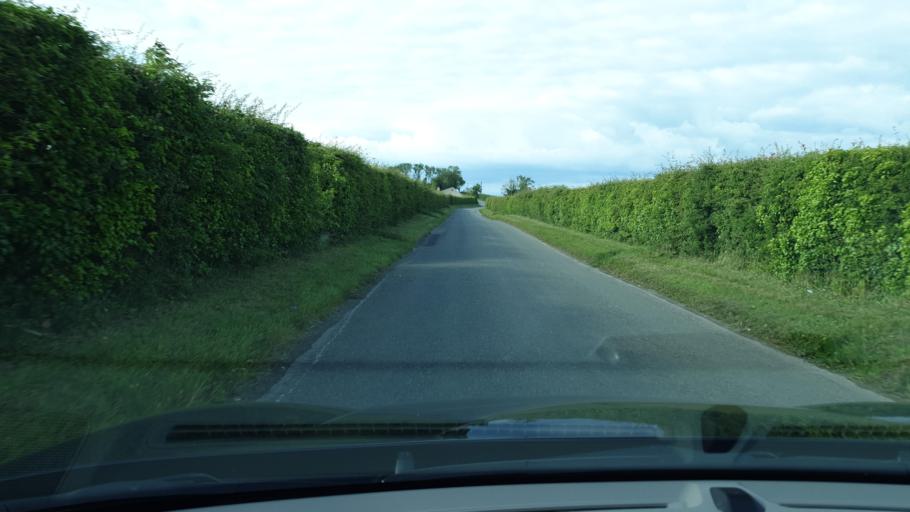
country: IE
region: Leinster
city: Lusk
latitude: 53.5601
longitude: -6.1667
